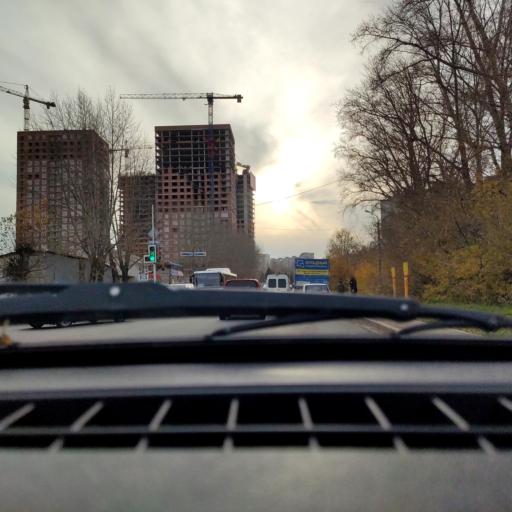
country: RU
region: Bashkortostan
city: Ufa
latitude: 54.7866
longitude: 56.0535
